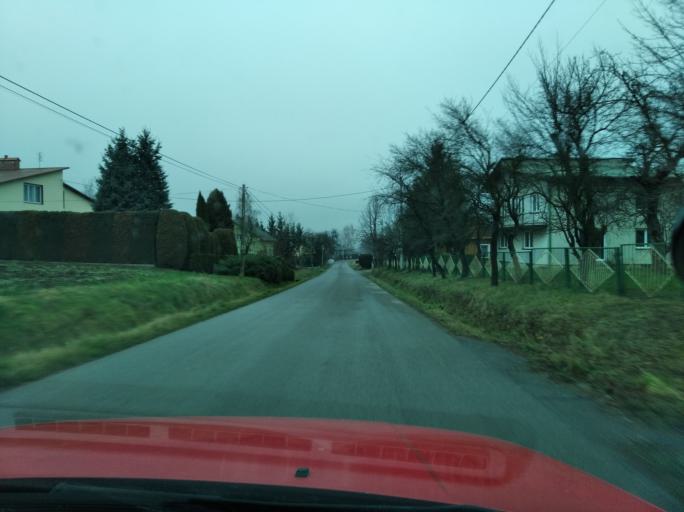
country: PL
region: Subcarpathian Voivodeship
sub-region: Powiat jaroslawski
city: Wierzbna
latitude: 50.0241
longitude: 22.6001
